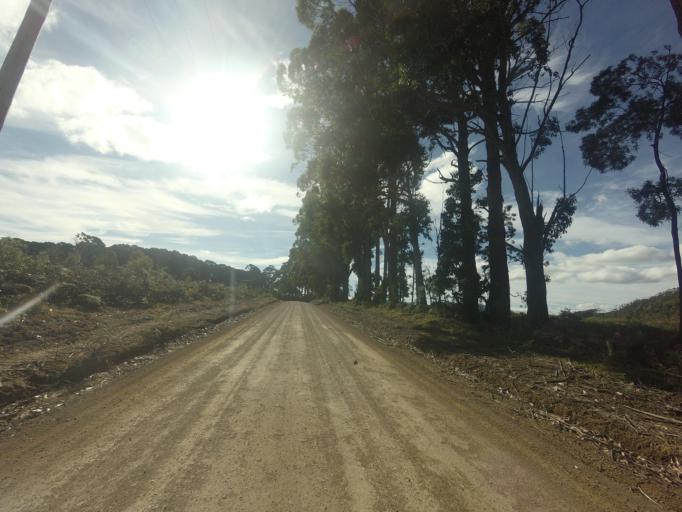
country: AU
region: Tasmania
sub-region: Clarence
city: Sandford
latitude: -43.1710
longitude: 147.7691
